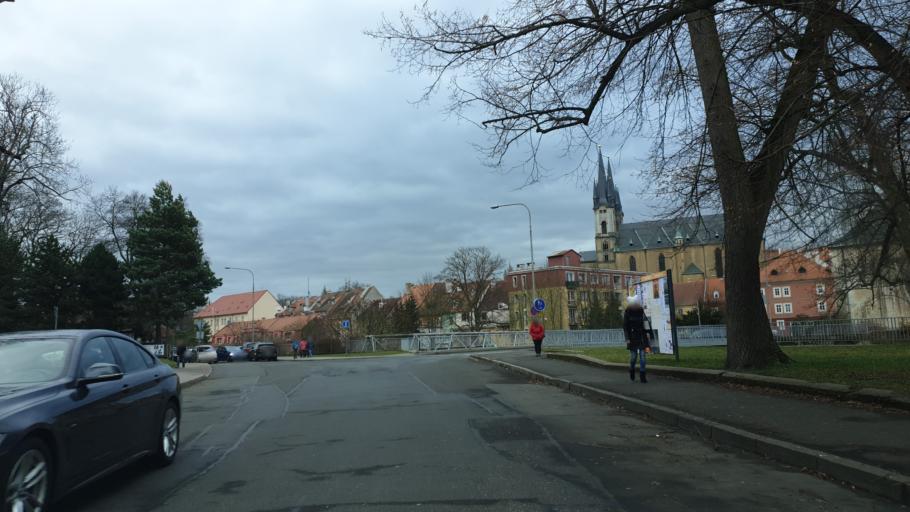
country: CZ
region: Karlovarsky
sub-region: Okres Cheb
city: Cheb
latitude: 50.0831
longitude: 12.3689
